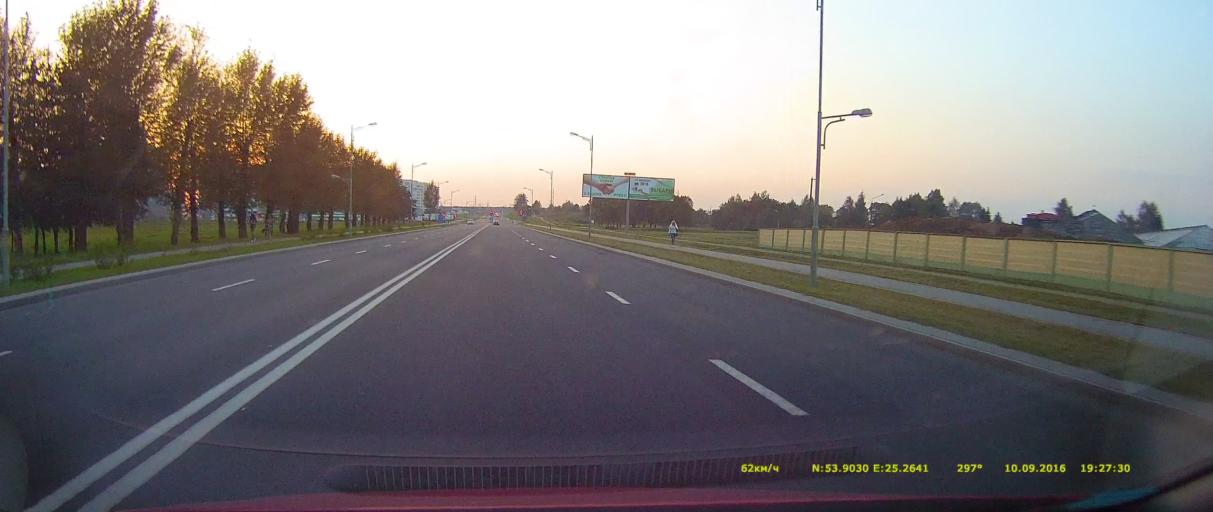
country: BY
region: Grodnenskaya
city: Lida
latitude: 53.9031
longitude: 25.2642
